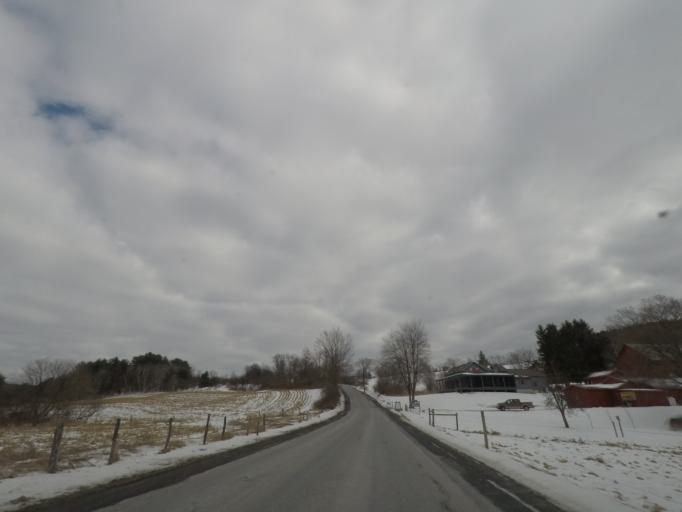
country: US
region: New York
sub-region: Rensselaer County
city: Hoosick Falls
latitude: 42.8734
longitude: -73.4008
